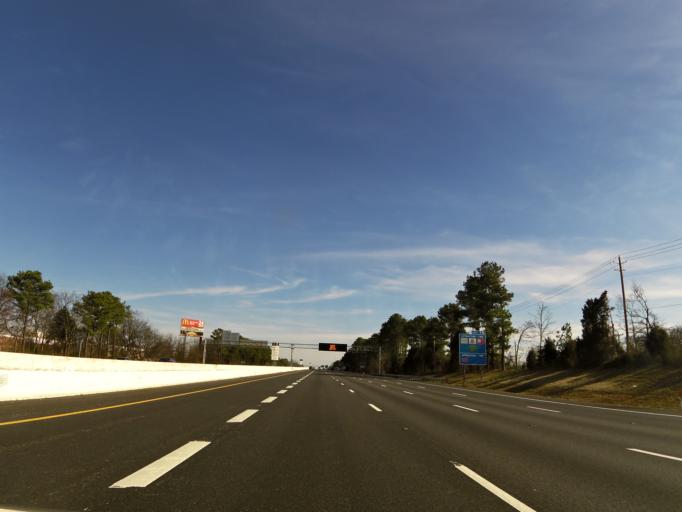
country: US
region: Tennessee
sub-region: Rutherford County
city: Murfreesboro
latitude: 35.8613
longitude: -86.4510
